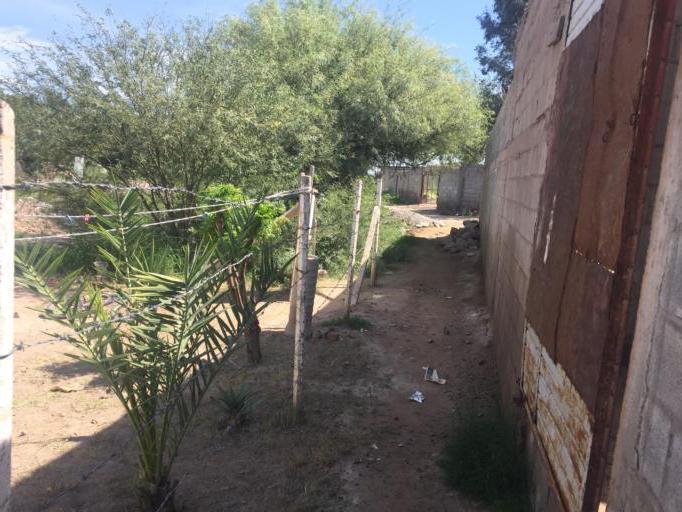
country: MX
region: Coahuila
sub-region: Matamoros
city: Veinte de Noviembre
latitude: 25.7194
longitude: -103.3504
